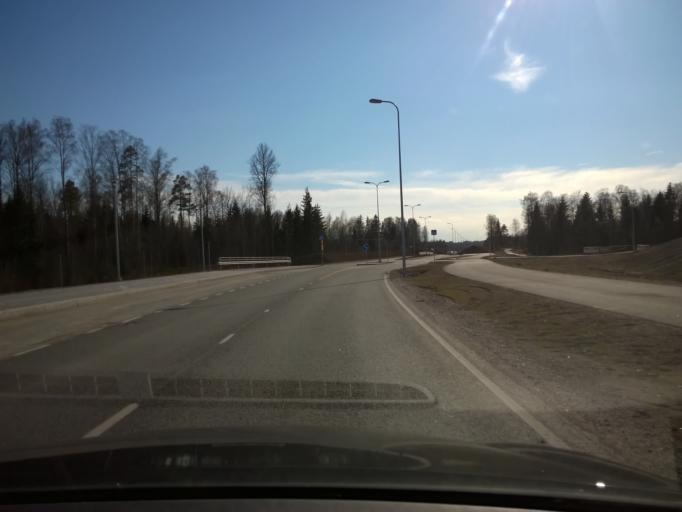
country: FI
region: Uusimaa
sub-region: Helsinki
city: Kilo
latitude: 60.1922
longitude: 24.7880
